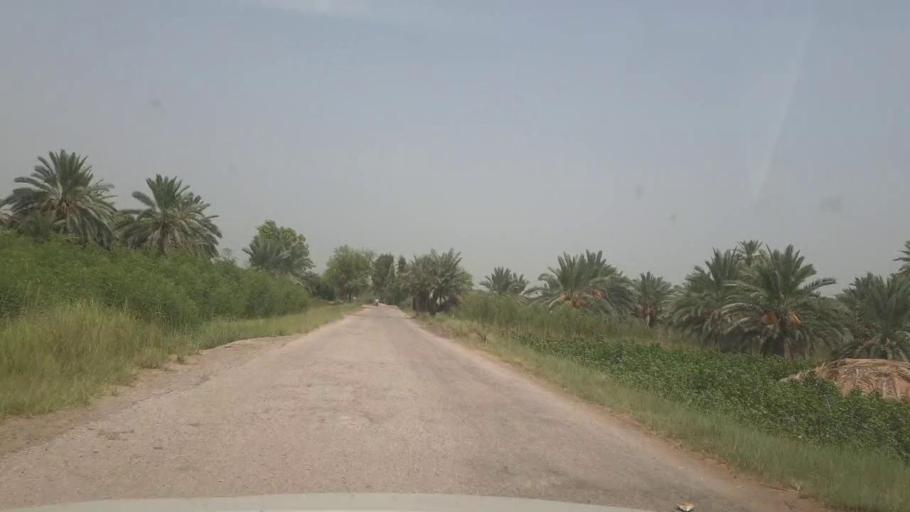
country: PK
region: Sindh
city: Kot Diji
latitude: 27.3640
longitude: 68.6628
